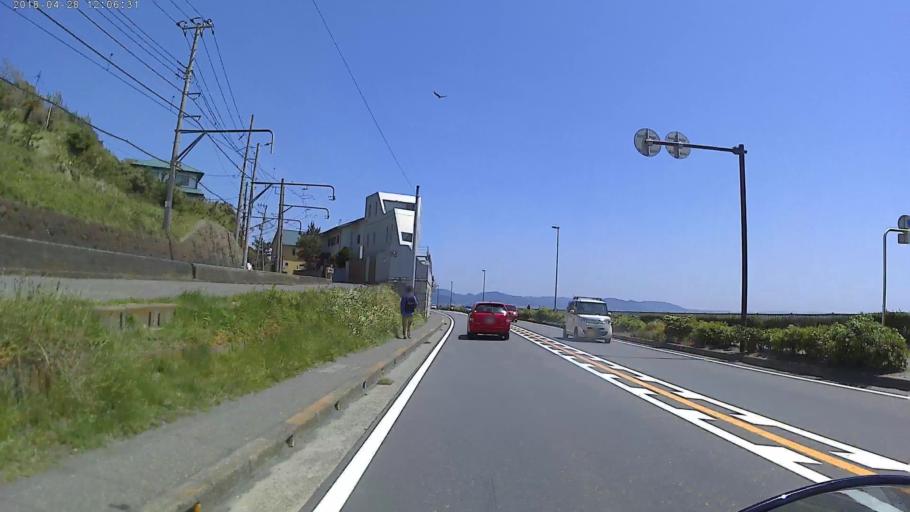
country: JP
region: Kanagawa
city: Kamakura
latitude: 35.3041
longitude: 139.5153
